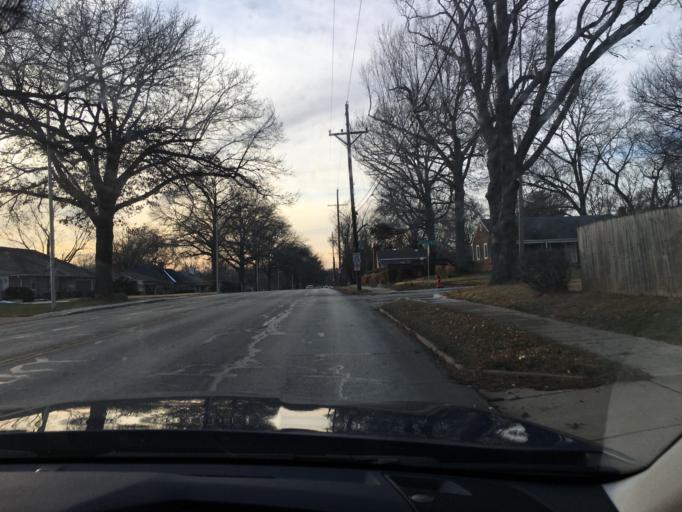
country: US
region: Kansas
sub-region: Johnson County
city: Leawood
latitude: 38.9746
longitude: -94.6017
